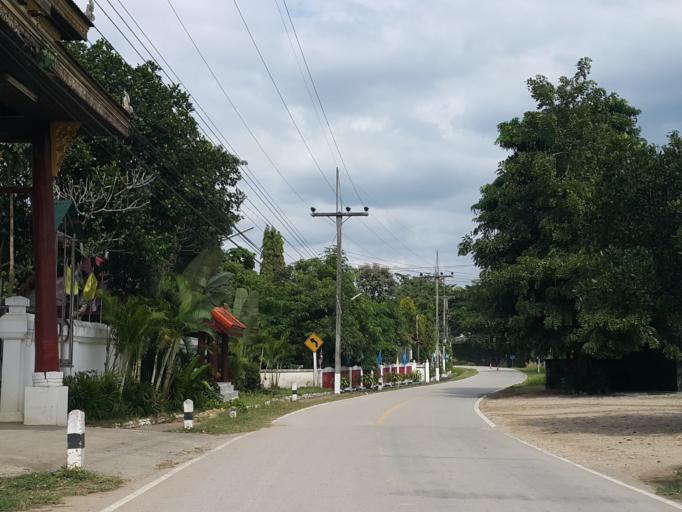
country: TH
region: Lampang
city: Chae Hom
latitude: 18.5602
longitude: 99.4577
